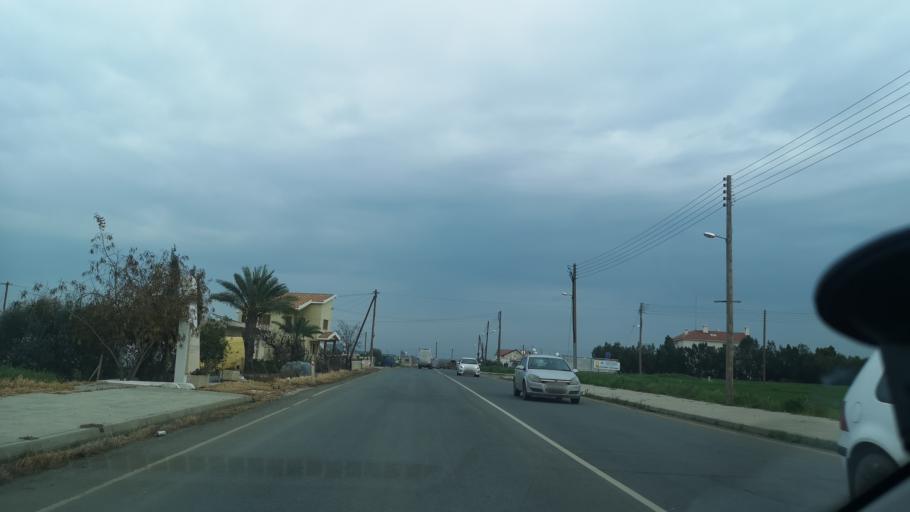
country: CY
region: Lefkosia
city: Tseri
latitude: 35.0766
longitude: 33.3141
